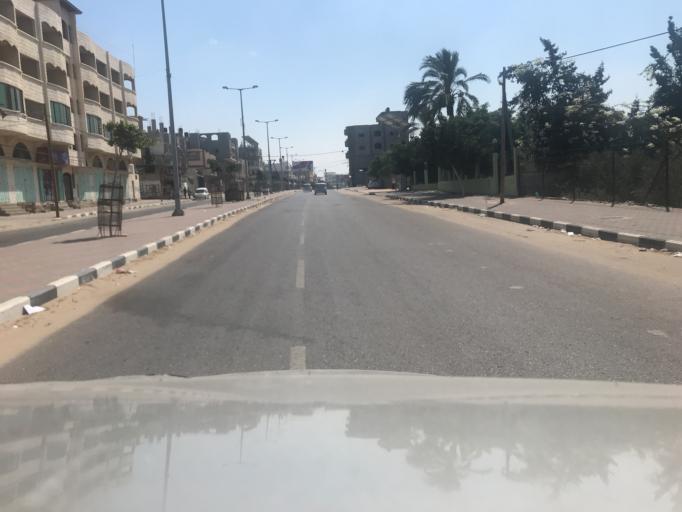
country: PS
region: Gaza Strip
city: Bayt Lahya
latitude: 31.5492
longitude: 34.4732
